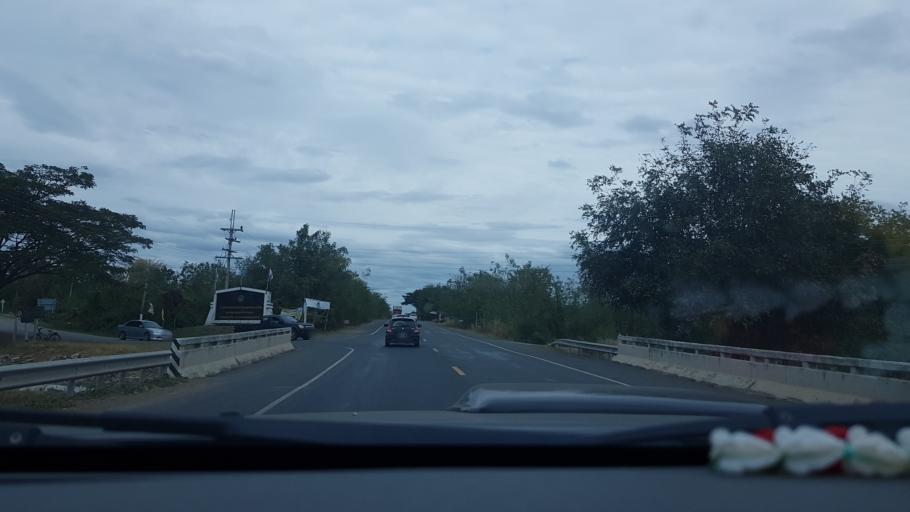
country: TH
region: Phetchabun
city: Phetchabun
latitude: 16.4650
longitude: 101.1236
